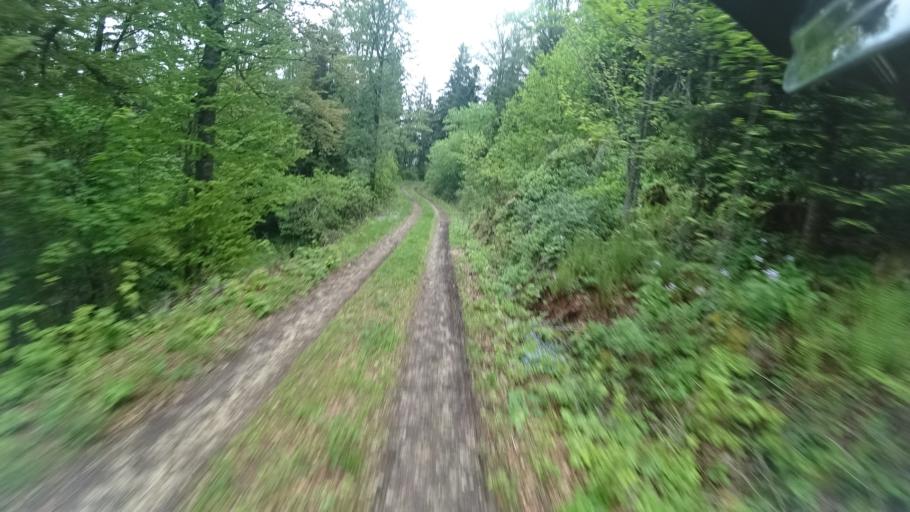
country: BA
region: Federation of Bosnia and Herzegovina
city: Bihac
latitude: 44.6311
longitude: 15.8134
